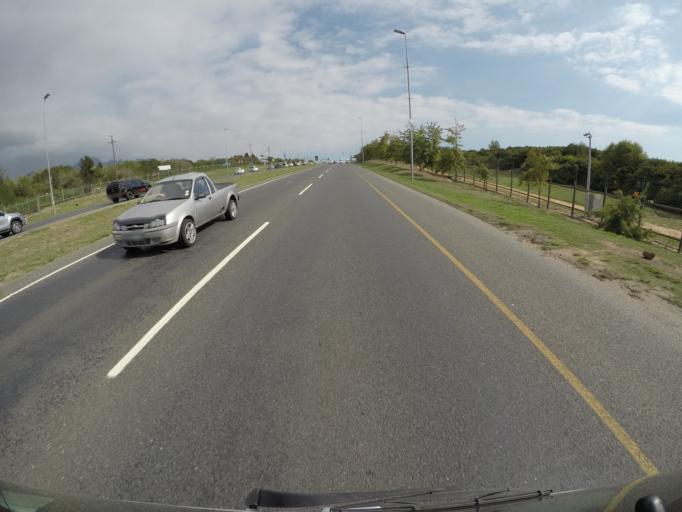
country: ZA
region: Western Cape
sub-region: Cape Winelands District Municipality
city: Stellenbosch
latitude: -33.9731
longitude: 18.8426
